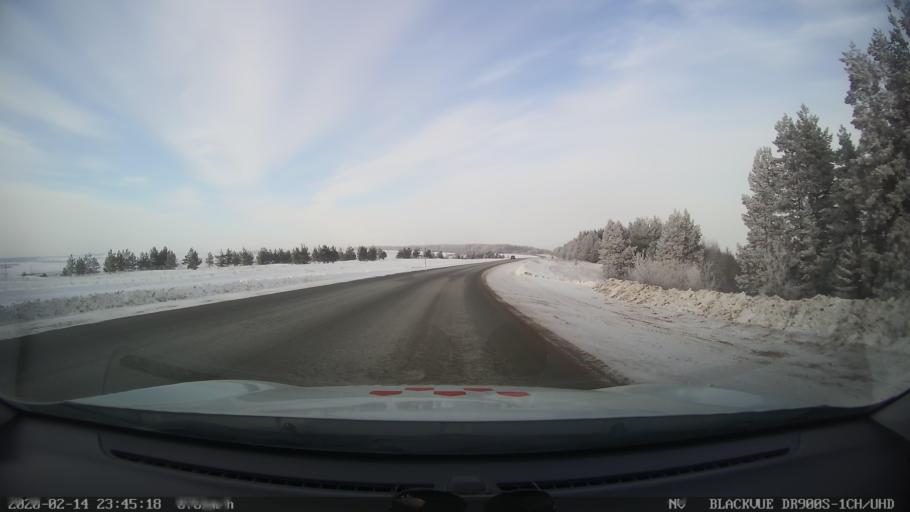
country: RU
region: Tatarstan
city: Kuybyshevskiy Zaton
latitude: 55.2189
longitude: 49.2317
